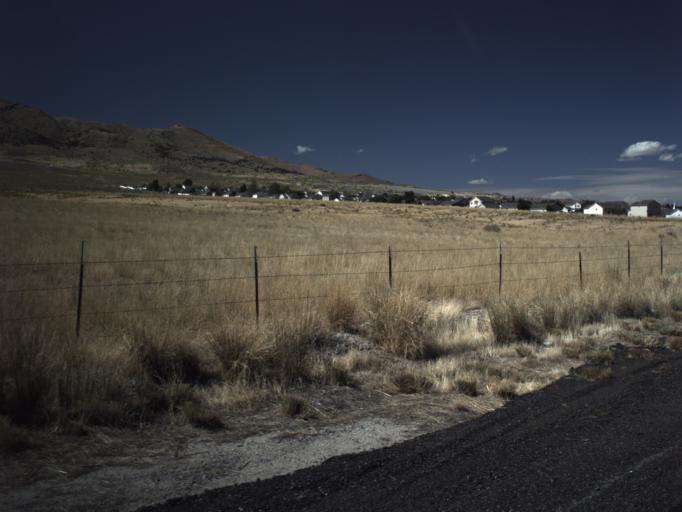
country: US
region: Utah
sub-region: Utah County
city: Saratoga Springs
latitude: 40.2831
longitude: -111.8731
